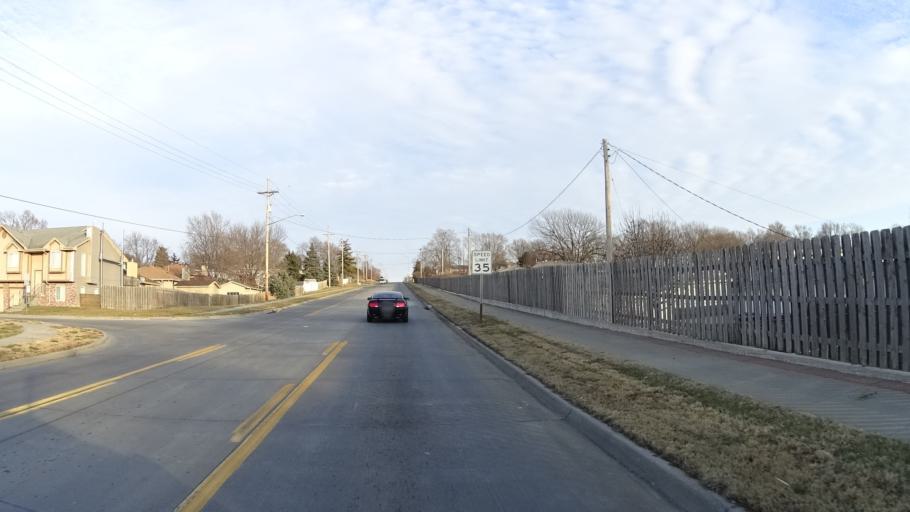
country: US
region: Nebraska
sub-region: Sarpy County
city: La Vista
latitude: 41.1907
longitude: -95.9998
